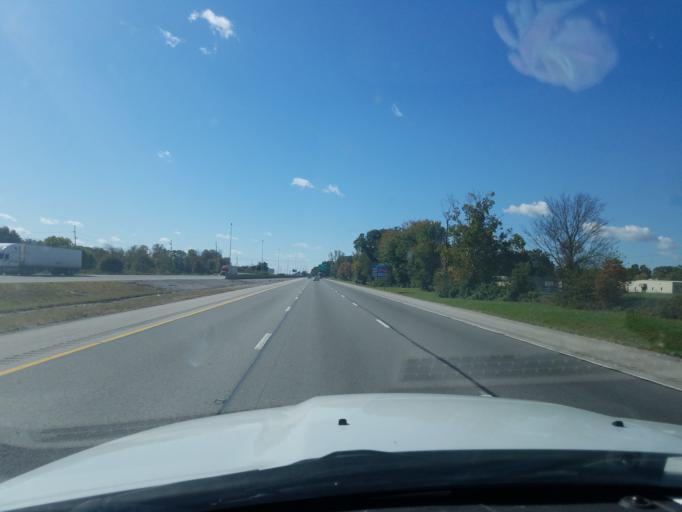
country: US
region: Kentucky
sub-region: Warren County
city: Bowling Green
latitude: 36.9541
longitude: -86.4059
